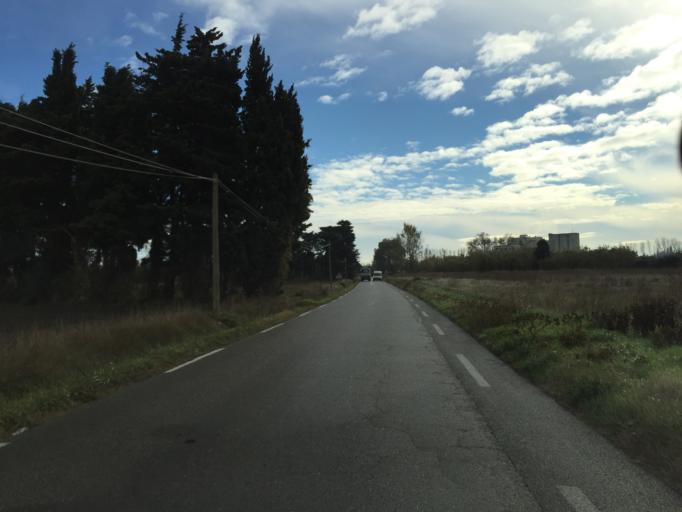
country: FR
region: Provence-Alpes-Cote d'Azur
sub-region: Departement du Vaucluse
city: Althen-des-Paluds
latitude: 43.9712
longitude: 4.9787
